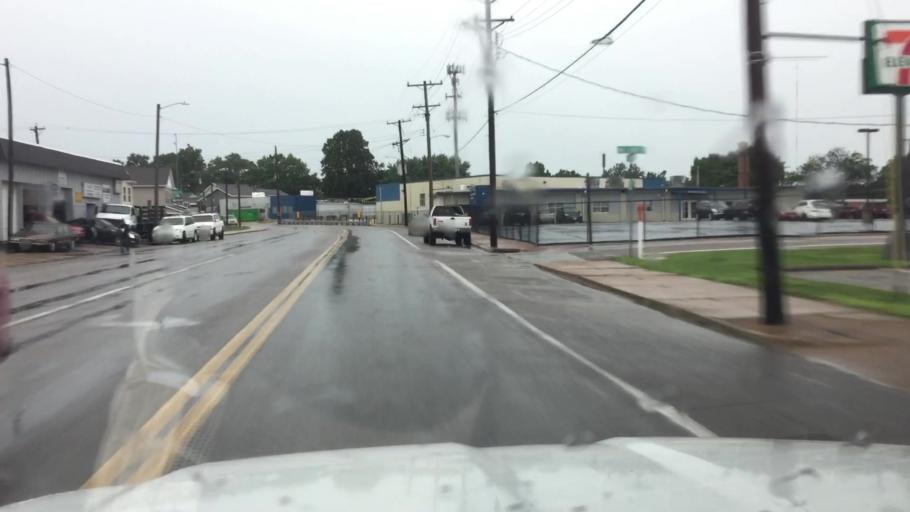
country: US
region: Missouri
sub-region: Saint Louis County
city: Lemay
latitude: 38.5333
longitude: -90.2756
